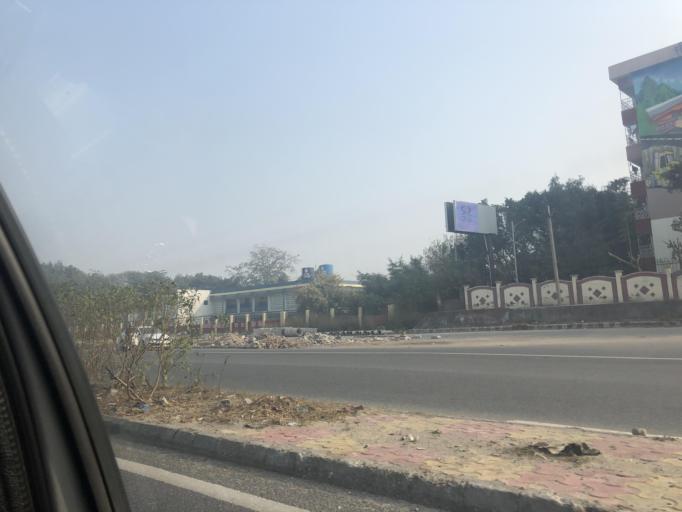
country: IN
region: NCT
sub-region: Central Delhi
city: Karol Bagh
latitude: 28.6152
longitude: 77.1365
